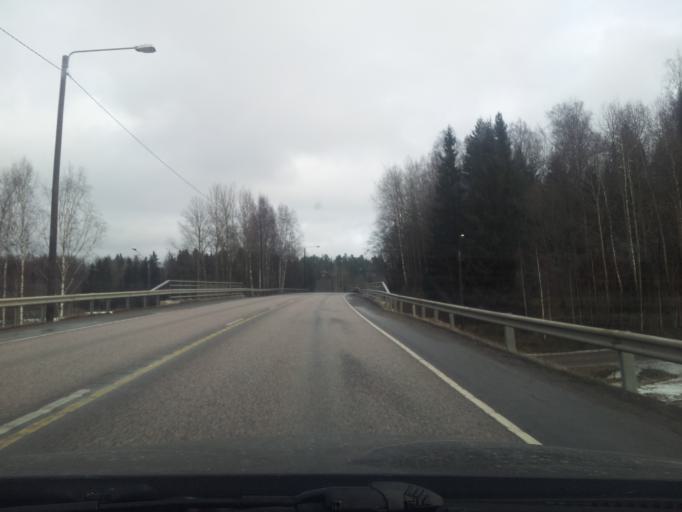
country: FI
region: Uusimaa
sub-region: Helsinki
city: Espoo
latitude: 60.1973
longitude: 24.5860
